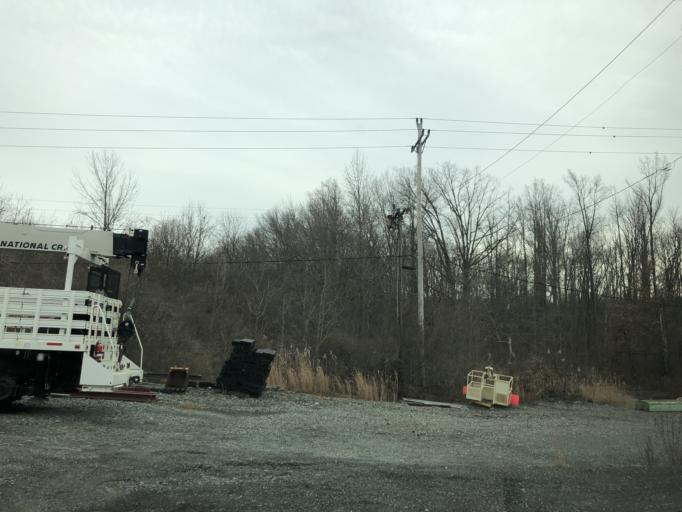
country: US
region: Delaware
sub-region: New Castle County
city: Newark
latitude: 39.6633
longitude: -75.7704
